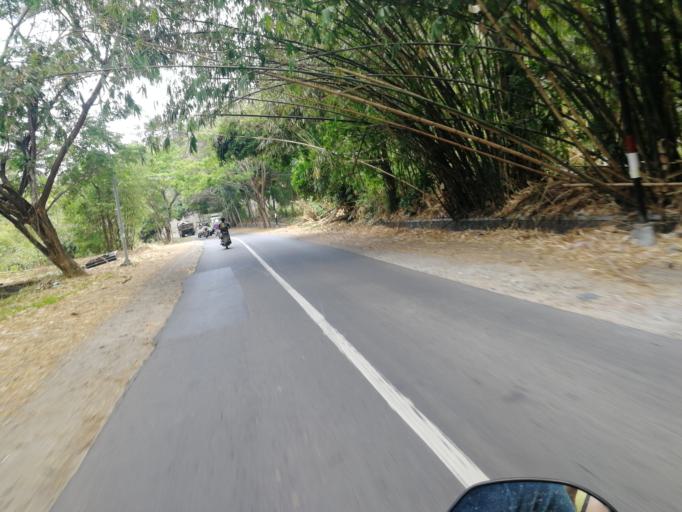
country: ID
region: West Nusa Tenggara
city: Karangsubagan
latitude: -8.4144
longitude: 116.0987
